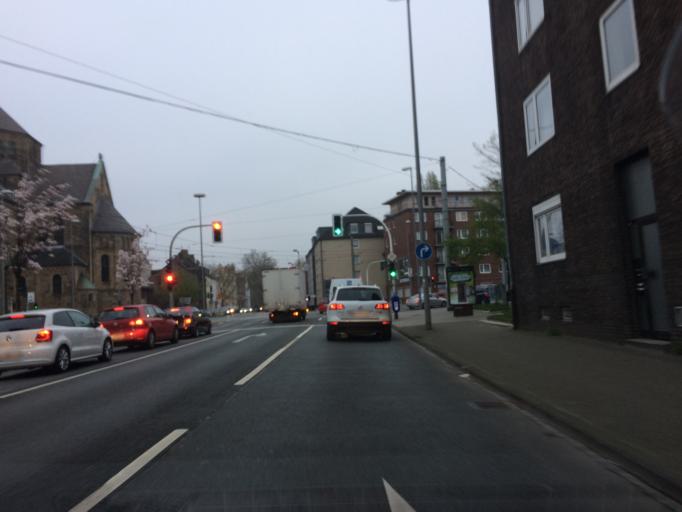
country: DE
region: North Rhine-Westphalia
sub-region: Regierungsbezirk Munster
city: Gelsenkirchen
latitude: 51.5142
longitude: 7.0963
